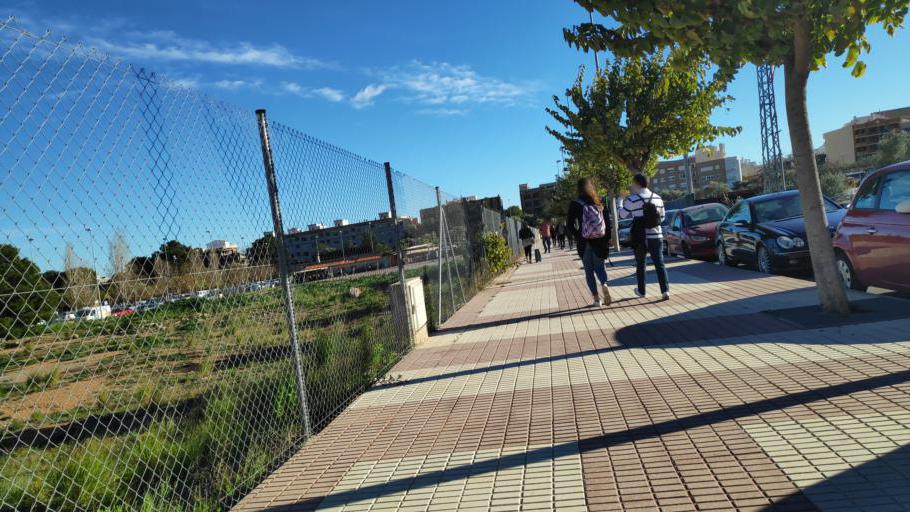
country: ES
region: Valencia
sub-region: Provincia de Castello
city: Benicassim
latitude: 40.0572
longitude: 0.0596
